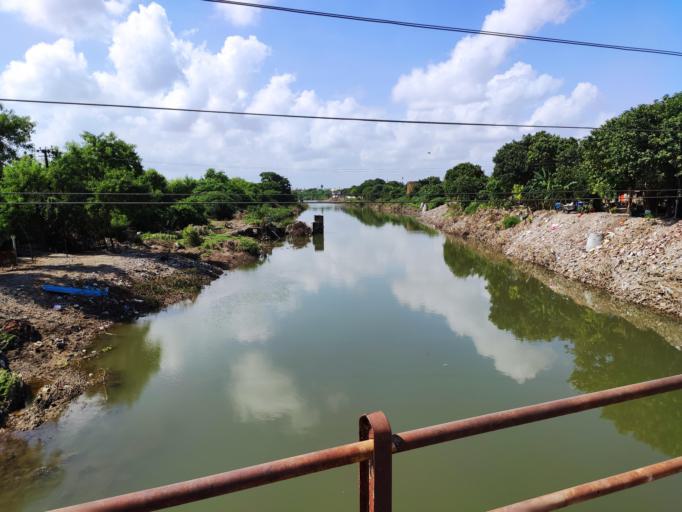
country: IN
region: Gujarat
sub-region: Jamnagar
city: Jamnagar
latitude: 22.4614
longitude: 70.0830
